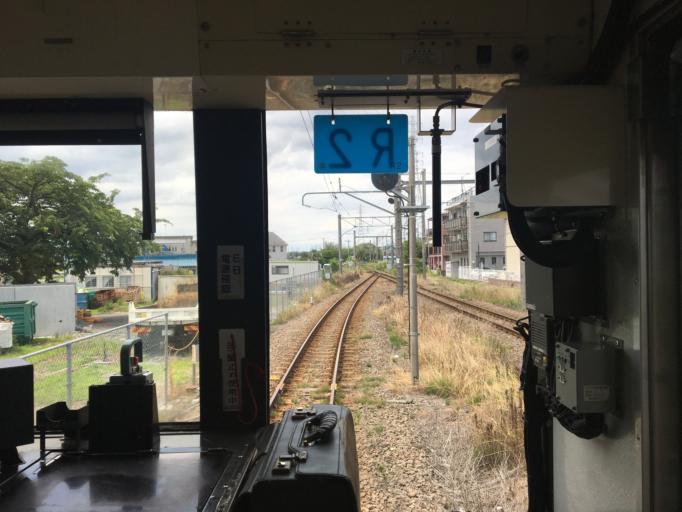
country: JP
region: Kanagawa
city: Zama
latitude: 35.4936
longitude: 139.3862
